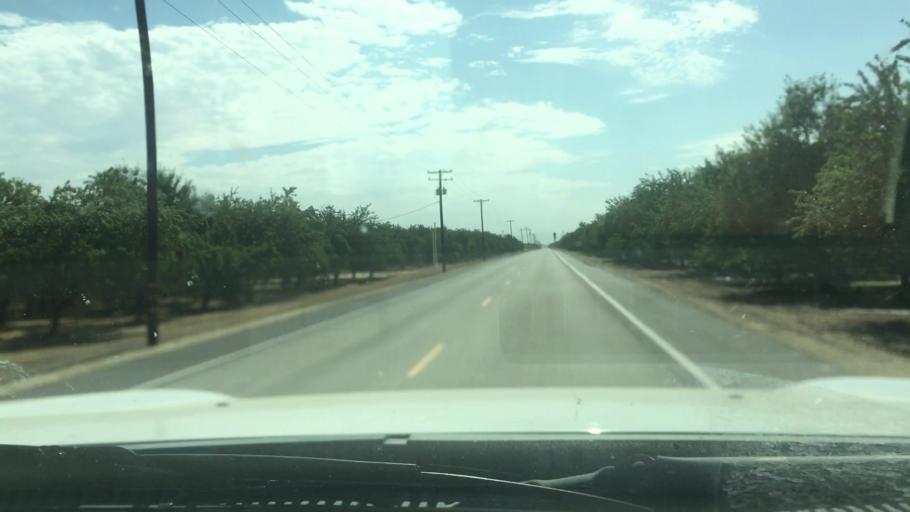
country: US
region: California
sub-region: Kern County
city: Wasco
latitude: 35.5577
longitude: -119.4621
